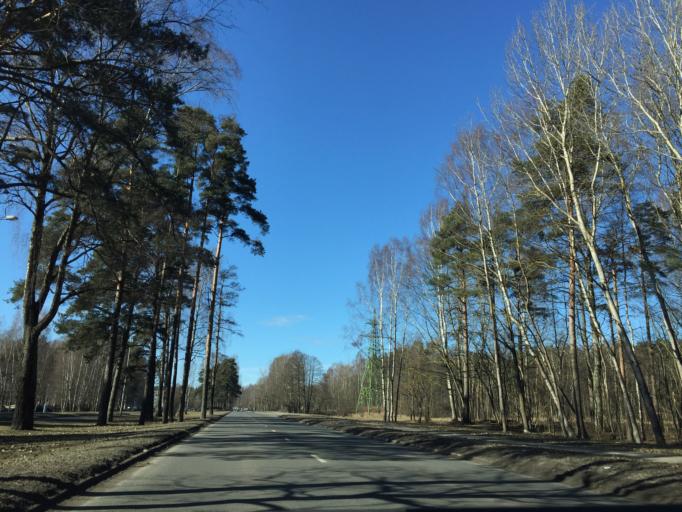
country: LV
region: Marupe
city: Marupe
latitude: 56.9666
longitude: 24.0227
